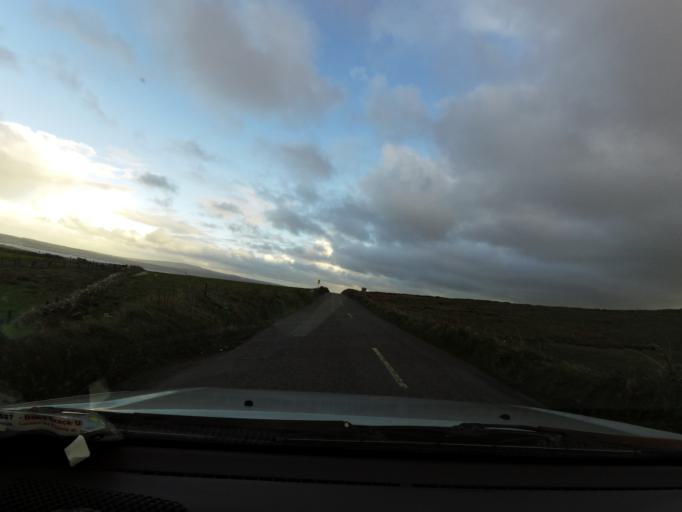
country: IE
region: Munster
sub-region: An Clar
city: Kilrush
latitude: 52.9601
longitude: -9.4228
